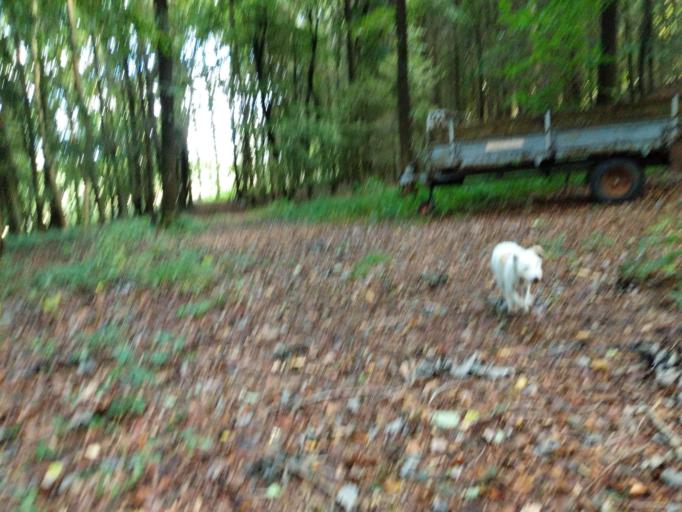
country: DE
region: Bavaria
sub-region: Lower Bavaria
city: Bad Abbach
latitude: 48.9600
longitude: 12.0526
